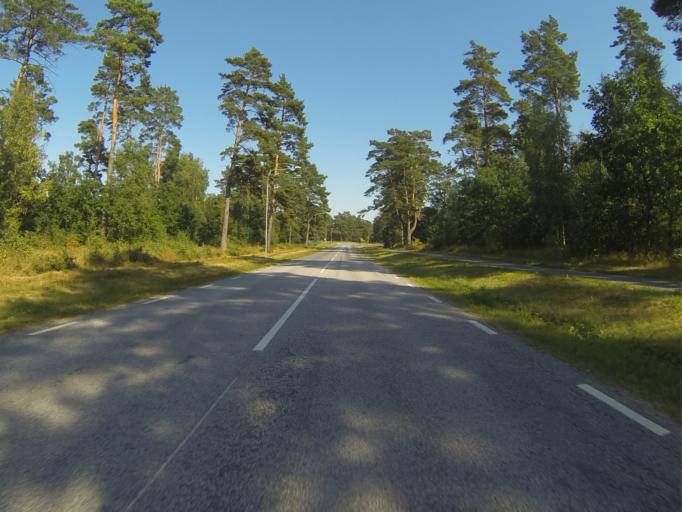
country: SE
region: Skane
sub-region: Hoors Kommun
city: Loberod
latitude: 55.7195
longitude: 13.4778
